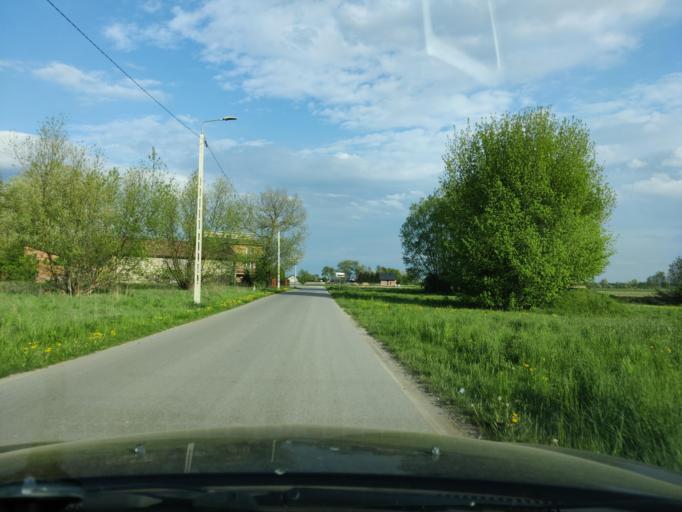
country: PL
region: Masovian Voivodeship
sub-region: Powiat piaseczynski
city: Konstancin-Jeziorna
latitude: 52.1212
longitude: 21.1605
